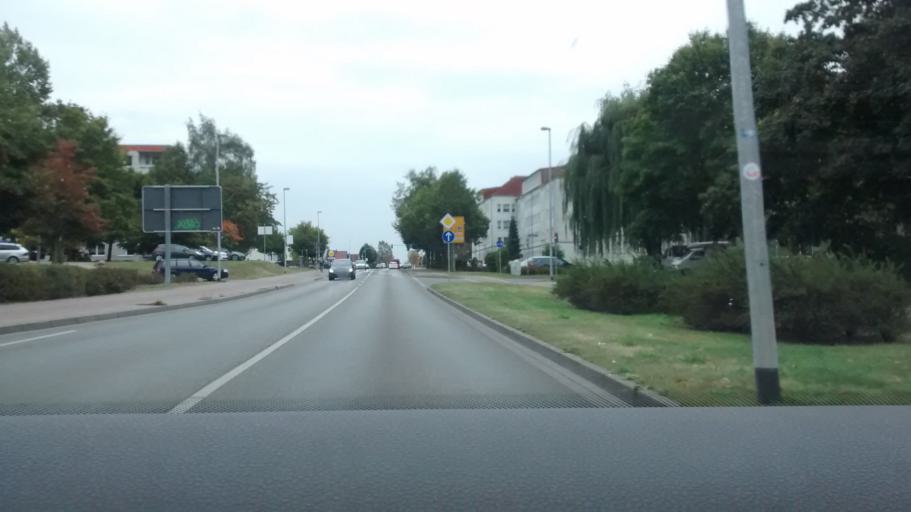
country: DE
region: Mecklenburg-Vorpommern
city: Wismar
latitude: 53.8966
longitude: 11.4234
